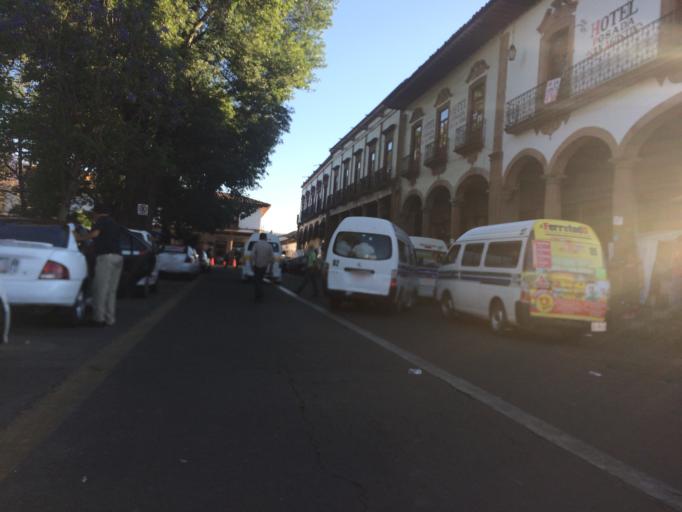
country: MX
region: Michoacan
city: Patzcuaro
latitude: 19.5165
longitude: -101.6091
